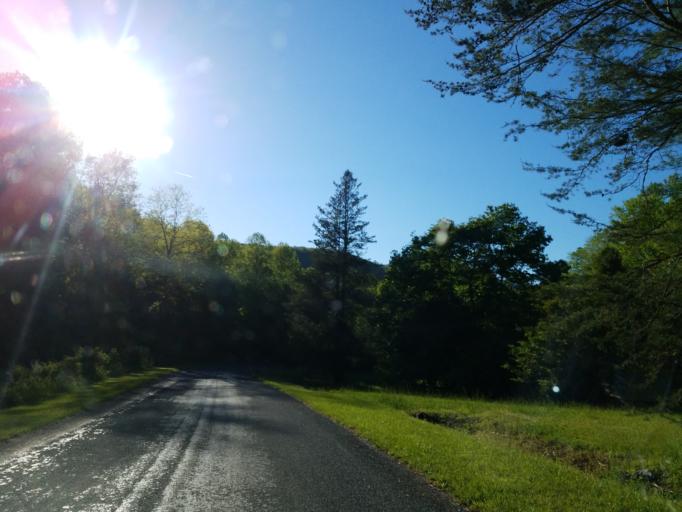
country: US
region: Georgia
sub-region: Fannin County
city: Blue Ridge
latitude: 34.7245
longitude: -84.2815
